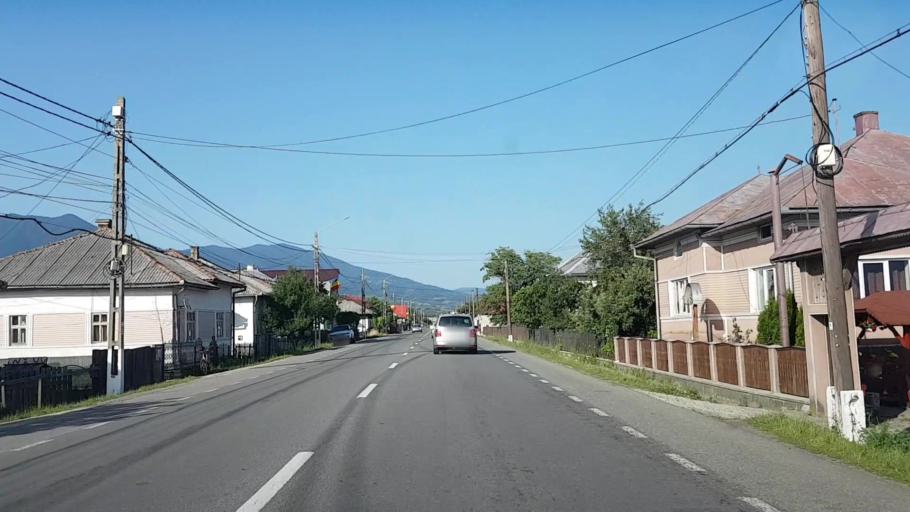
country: RO
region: Bistrita-Nasaud
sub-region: Comuna Josenii Bargaului
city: Josenii Bargaului
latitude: 47.2099
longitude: 24.6661
